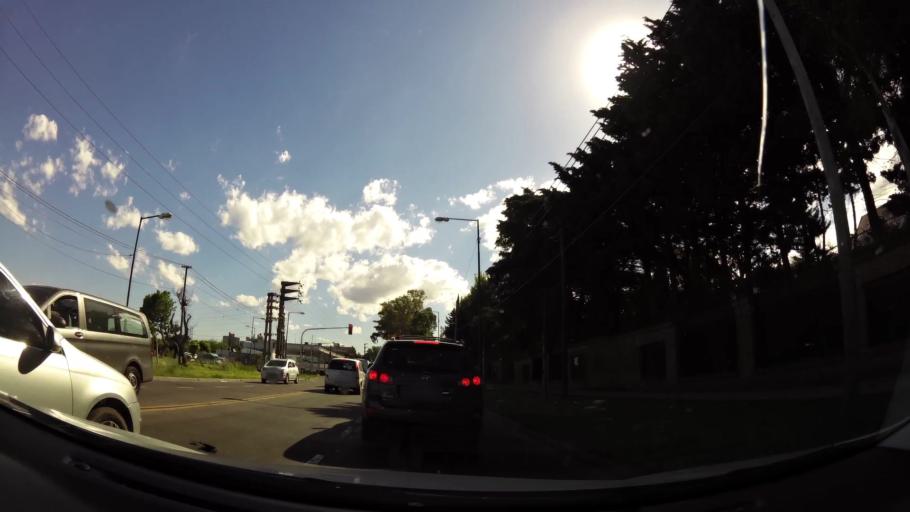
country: AR
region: Buenos Aires
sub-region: Partido de Tigre
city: Tigre
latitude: -34.4655
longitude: -58.5544
